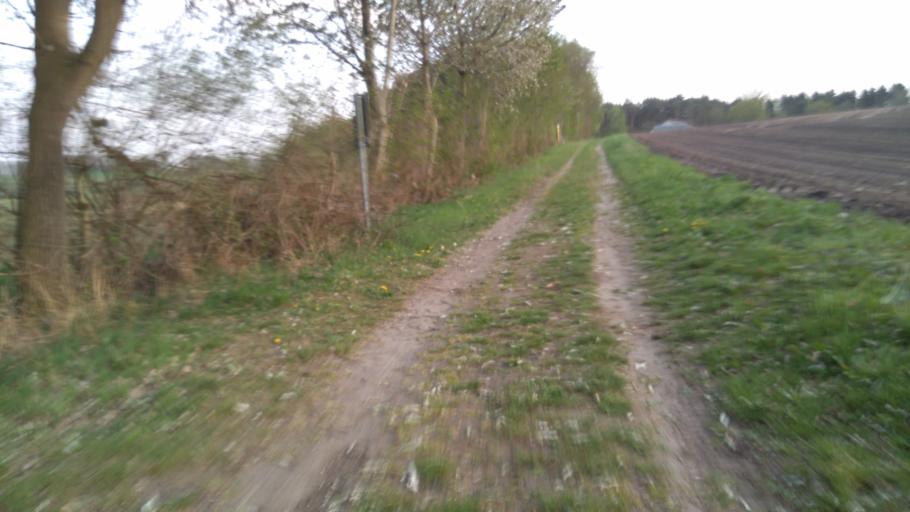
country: DE
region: Lower Saxony
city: Bliedersdorf
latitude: 53.4857
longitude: 9.5575
